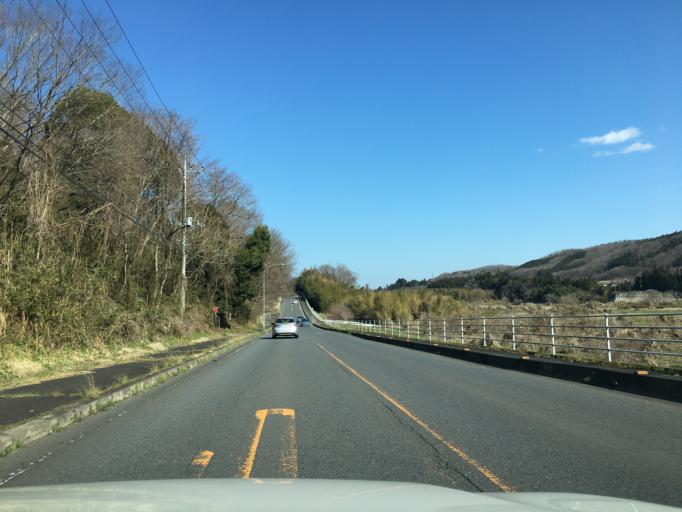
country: JP
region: Tochigi
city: Motegi
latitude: 36.5618
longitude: 140.2605
